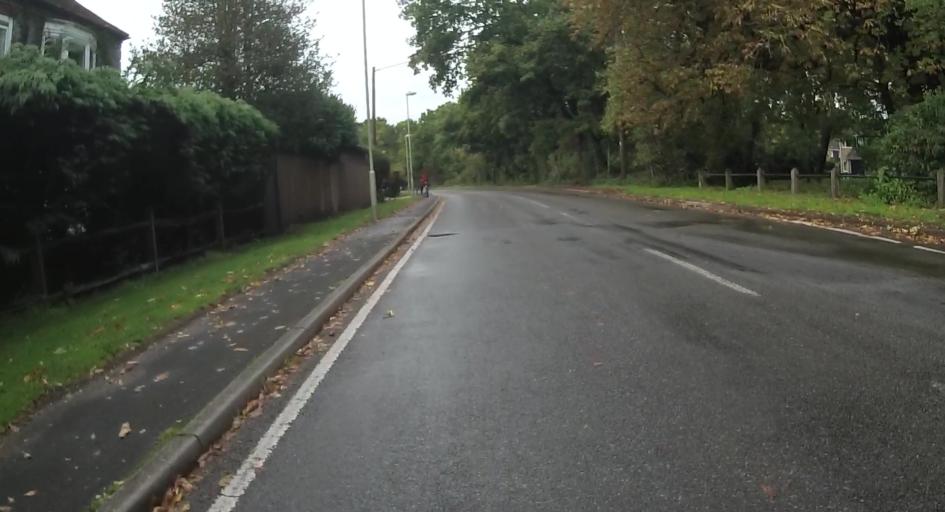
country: GB
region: England
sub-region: Hampshire
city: Tadley
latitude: 51.3532
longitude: -1.1689
